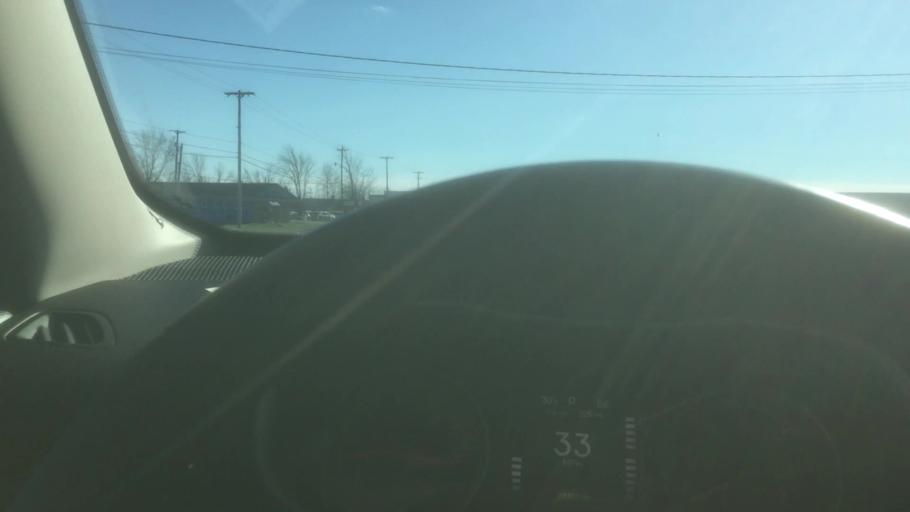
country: US
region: Michigan
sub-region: Bay County
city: Bay City
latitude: 43.5798
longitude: -83.8568
